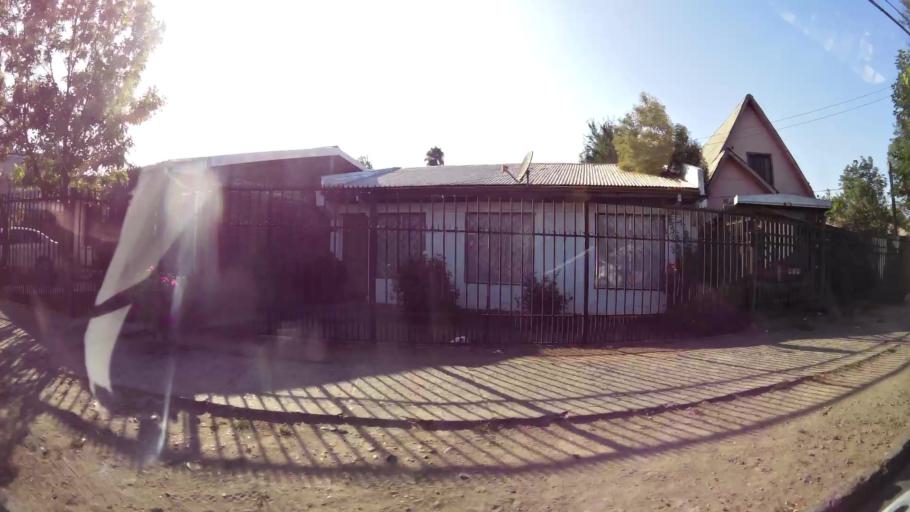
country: CL
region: Maule
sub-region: Provincia de Talca
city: Talca
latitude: -35.4087
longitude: -71.6592
